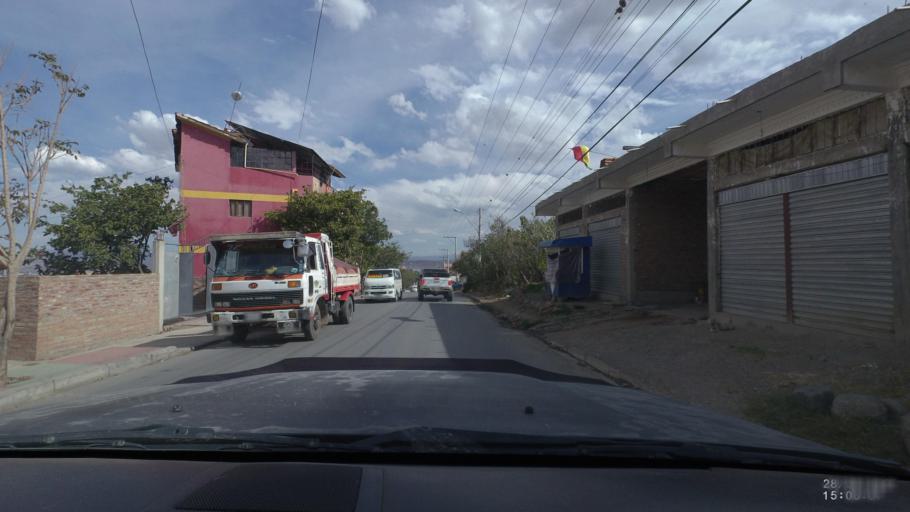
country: BO
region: Cochabamba
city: Cochabamba
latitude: -17.3365
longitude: -66.2842
